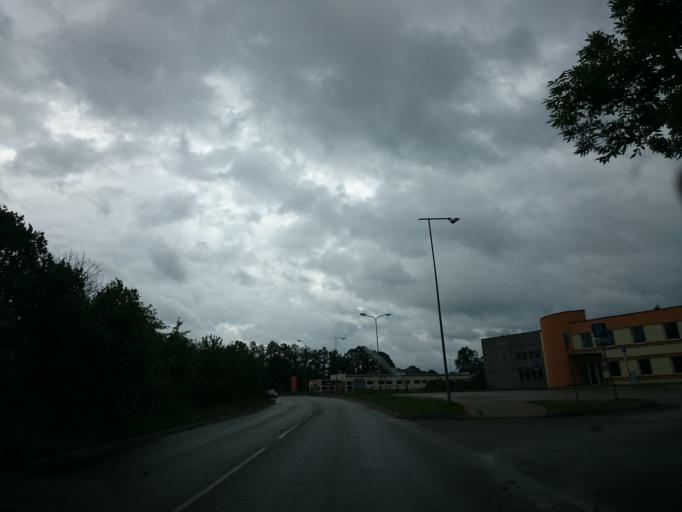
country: LV
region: Cesu Rajons
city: Cesis
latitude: 57.3138
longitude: 25.2970
